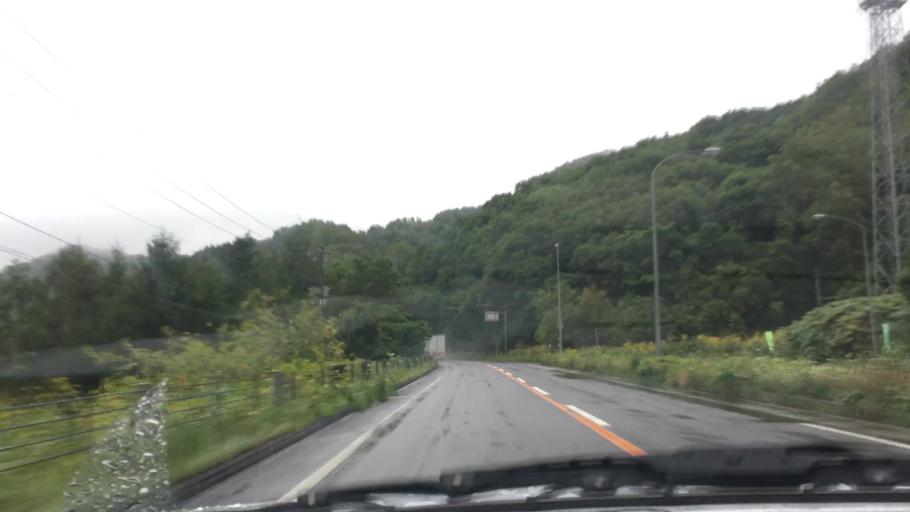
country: JP
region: Hokkaido
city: Niseko Town
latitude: 42.6026
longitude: 140.6185
